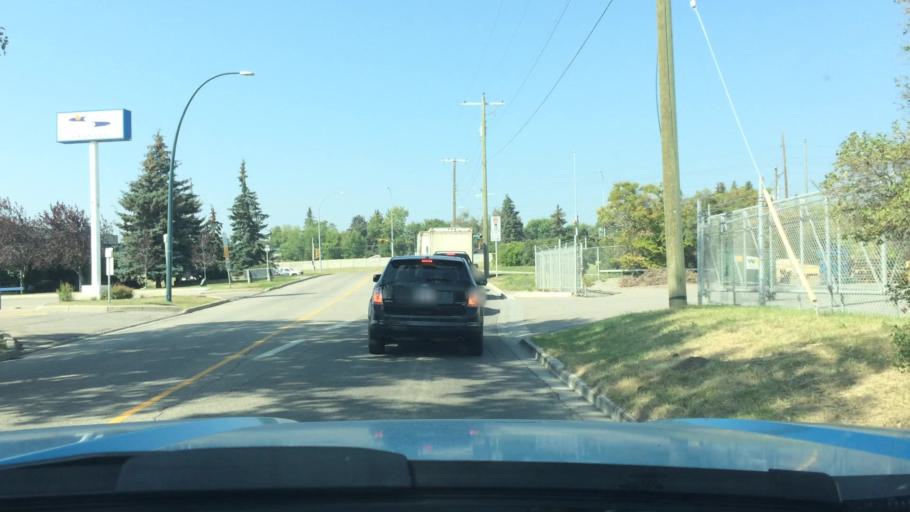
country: CA
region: Alberta
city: Calgary
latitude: 50.9886
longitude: -114.0518
